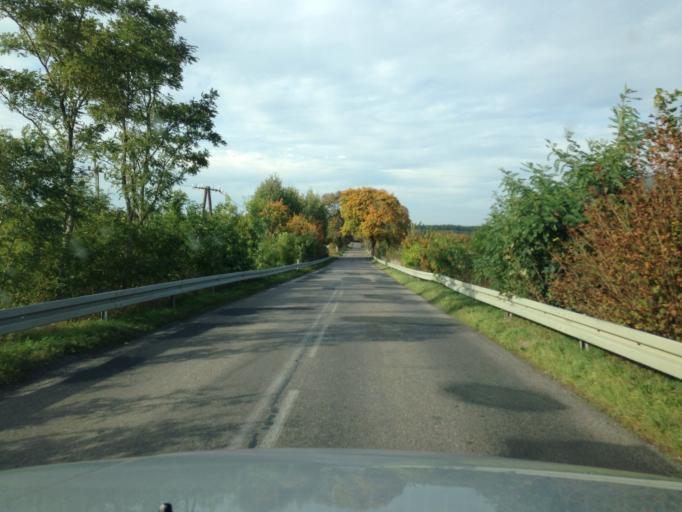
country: PL
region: Pomeranian Voivodeship
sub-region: Powiat koscierski
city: Koscierzyna
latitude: 54.0777
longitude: 18.0029
